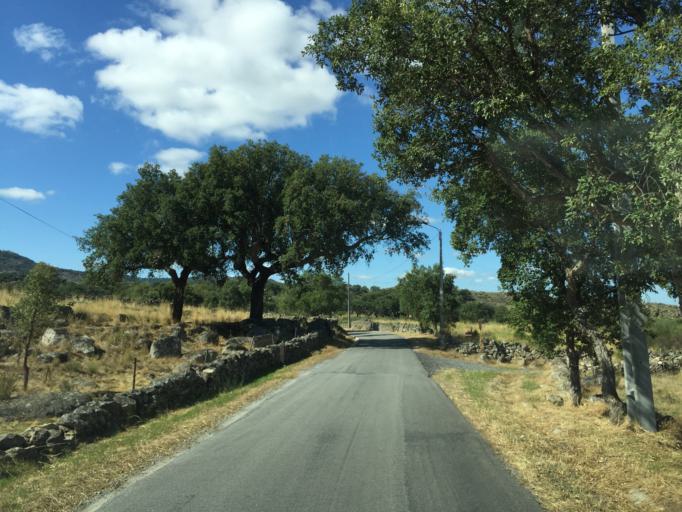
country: PT
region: Portalegre
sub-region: Marvao
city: Marvao
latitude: 39.4223
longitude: -7.3578
